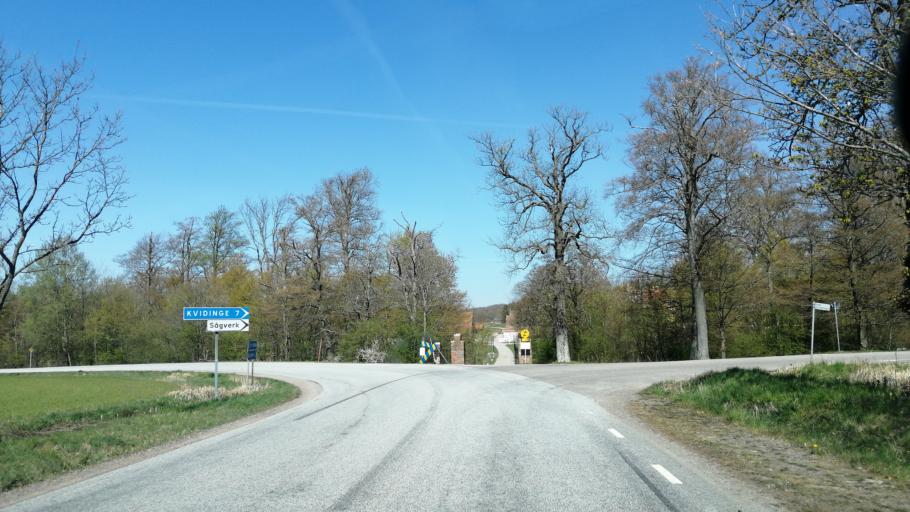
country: SE
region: Skane
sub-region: Astorps Kommun
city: Astorp
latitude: 56.1015
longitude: 12.9692
